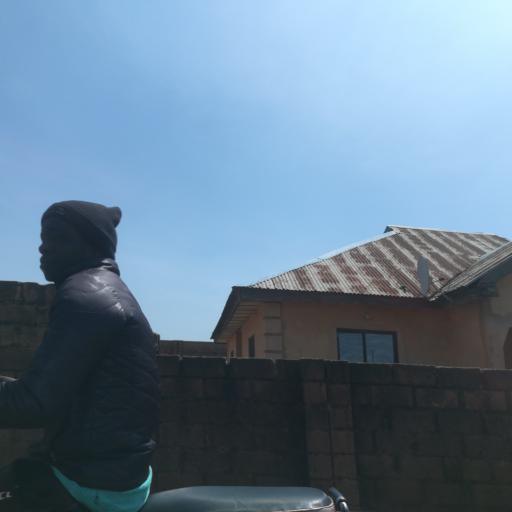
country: NG
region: Plateau
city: Bukuru
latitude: 9.8423
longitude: 8.9058
